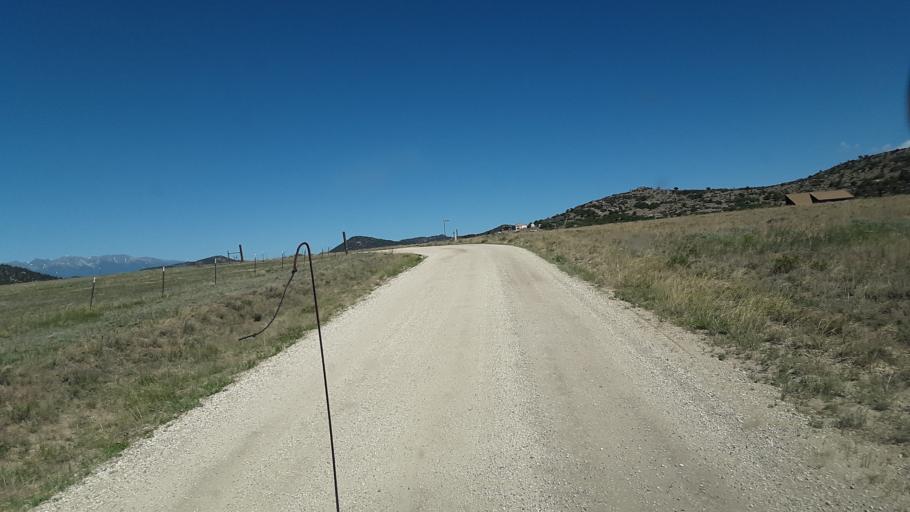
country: US
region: Colorado
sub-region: Custer County
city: Westcliffe
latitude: 38.2380
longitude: -105.4907
